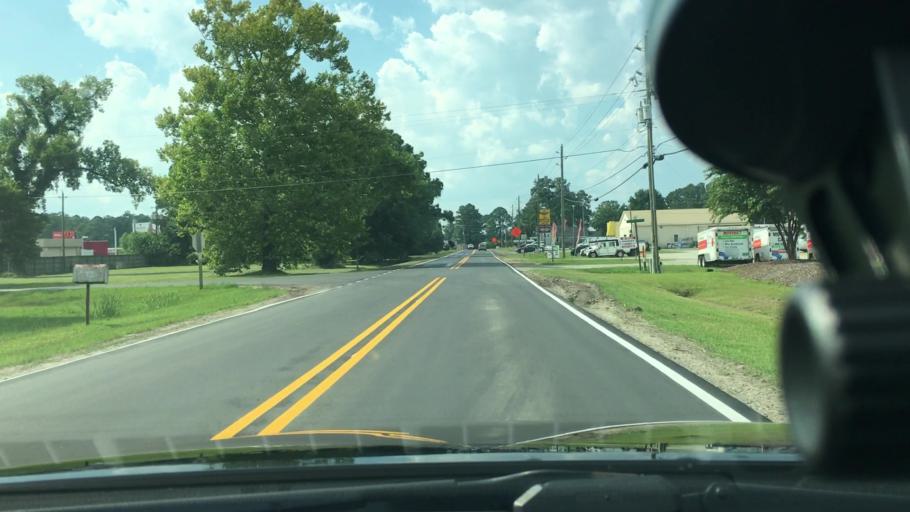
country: US
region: North Carolina
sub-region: Craven County
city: James City
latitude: 35.0748
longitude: -77.0253
